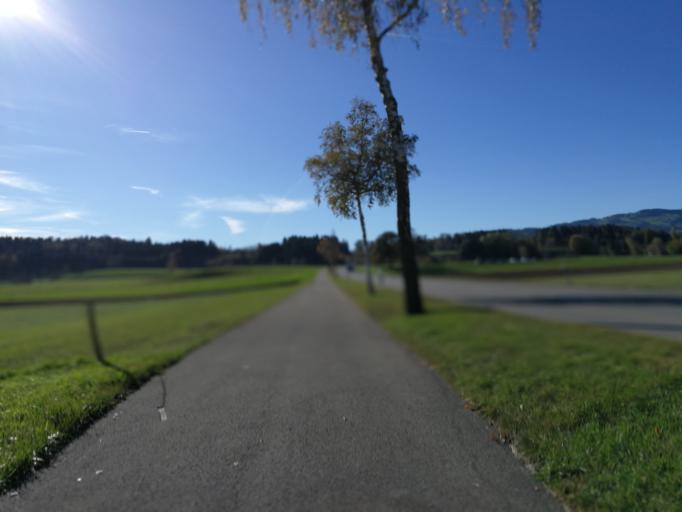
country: CH
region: Zurich
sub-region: Bezirk Hinwil
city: Gossau
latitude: 47.2998
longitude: 8.7467
